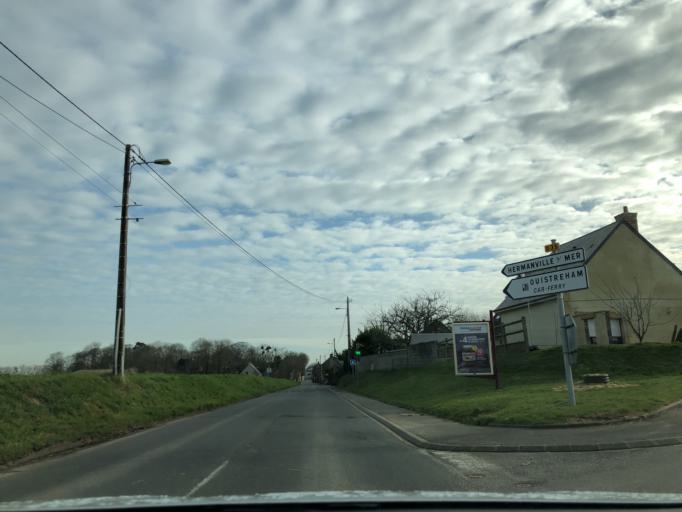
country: FR
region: Lower Normandy
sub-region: Departement du Calvados
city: Cresserons
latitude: 49.2918
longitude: -0.3585
